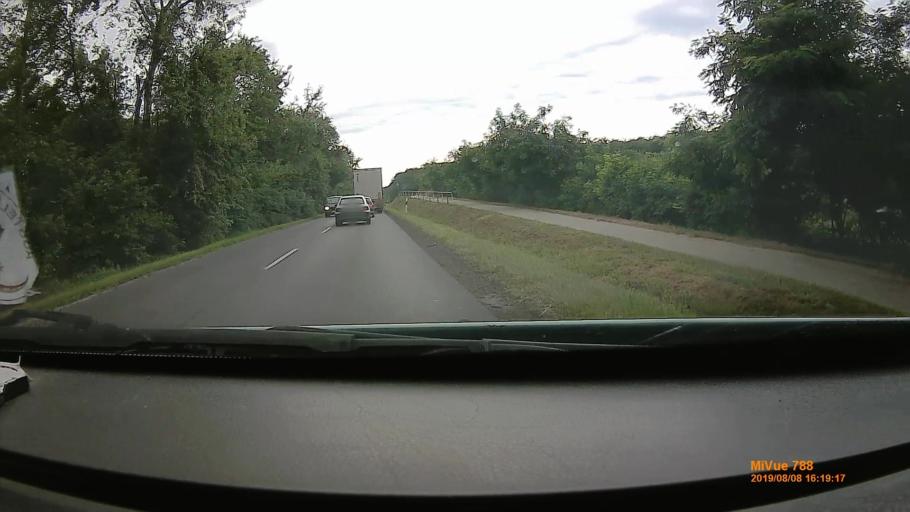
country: HU
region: Szabolcs-Szatmar-Bereg
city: Mateszalka
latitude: 47.9658
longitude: 22.2767
